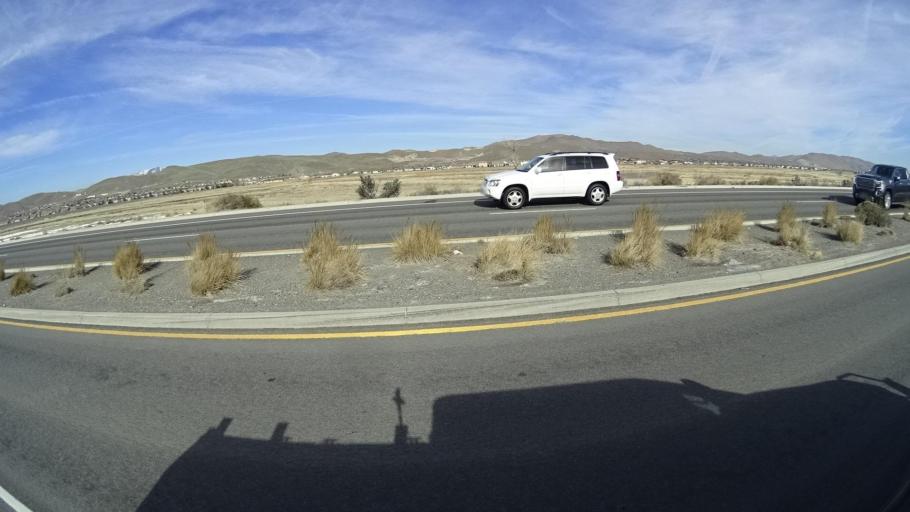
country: US
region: Nevada
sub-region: Washoe County
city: Spanish Springs
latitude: 39.5990
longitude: -119.7128
